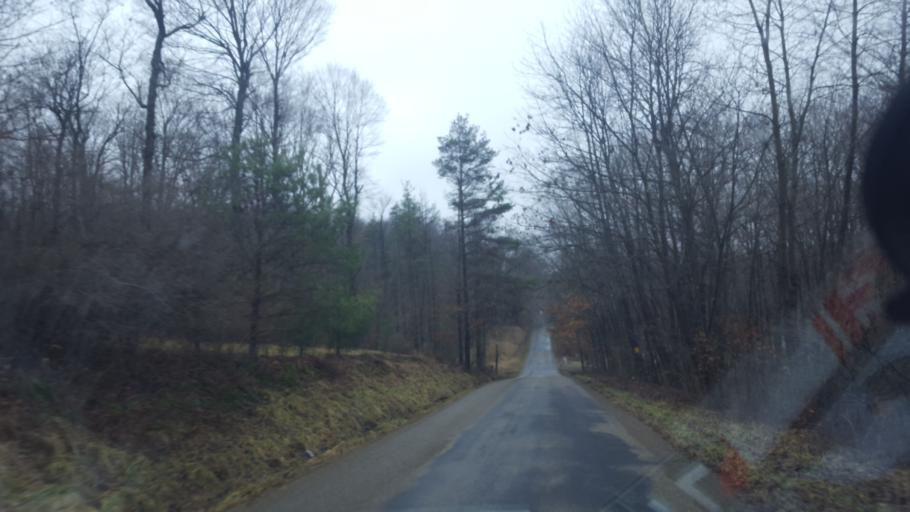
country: US
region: Ohio
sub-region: Sandusky County
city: Bellville
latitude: 40.5728
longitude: -82.3943
